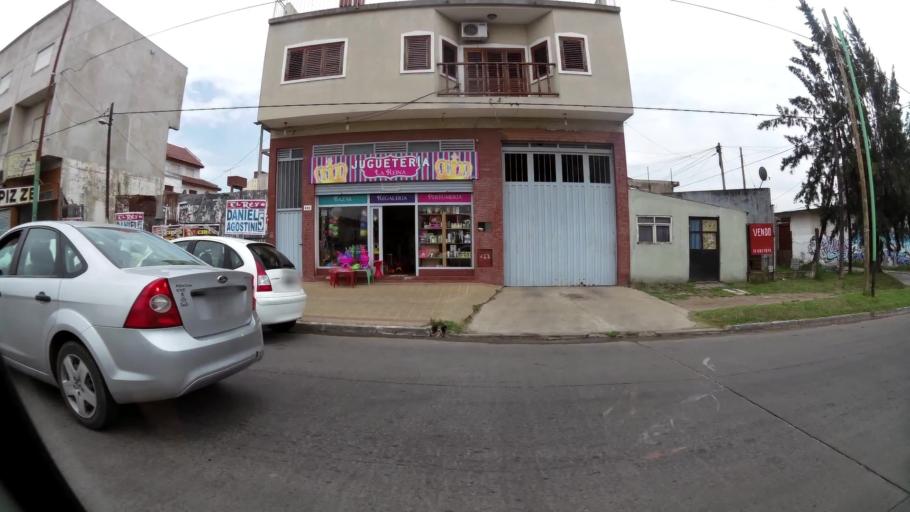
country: AR
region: Buenos Aires
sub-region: Partido de La Plata
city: La Plata
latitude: -34.9064
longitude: -57.9885
